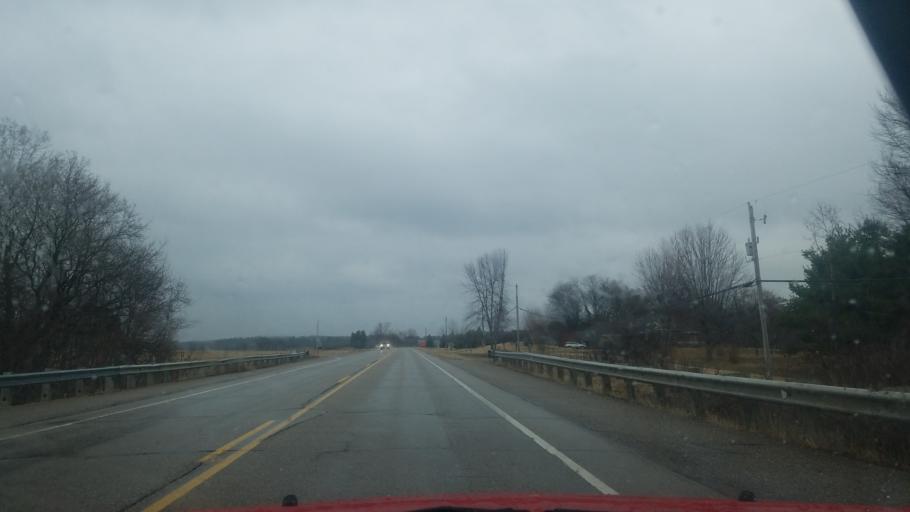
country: US
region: Wisconsin
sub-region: Dunn County
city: Tainter Lake
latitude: 44.9543
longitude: -91.9022
